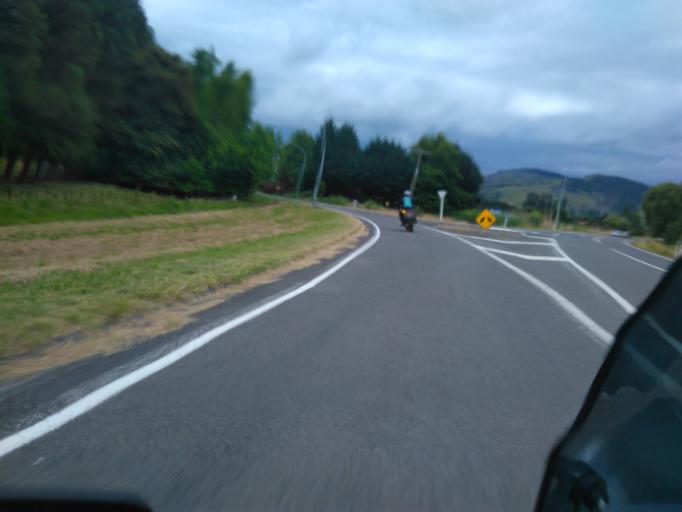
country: NZ
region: Gisborne
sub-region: Gisborne District
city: Gisborne
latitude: -38.4749
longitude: 177.8619
